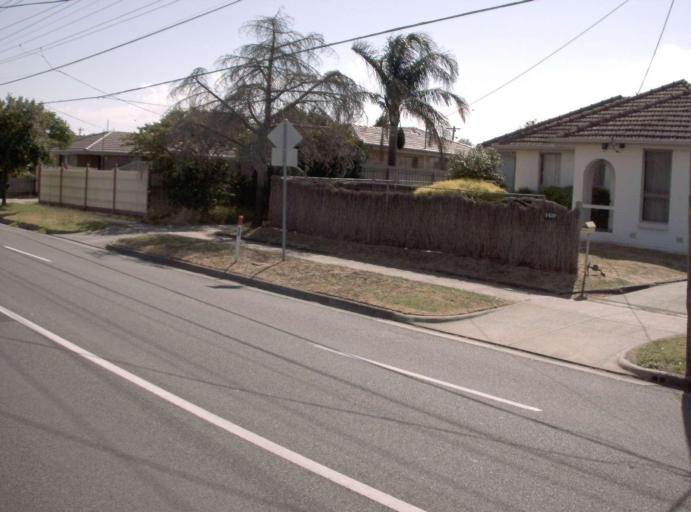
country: AU
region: Victoria
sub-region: Greater Dandenong
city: Keysborough
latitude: -37.9918
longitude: 145.1823
